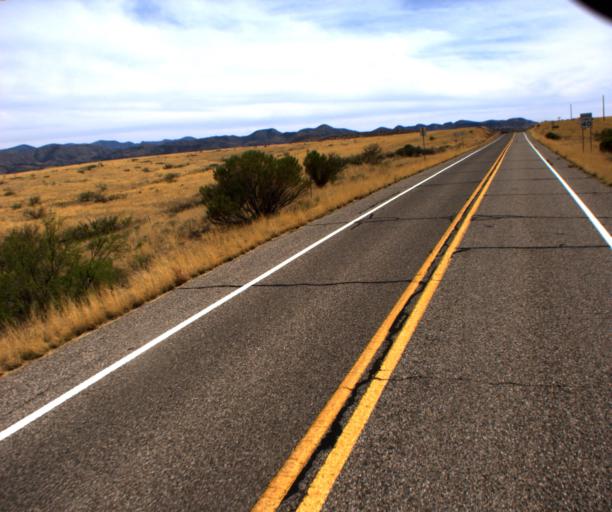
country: US
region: Arizona
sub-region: Cochise County
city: Willcox
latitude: 32.0108
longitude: -109.4400
